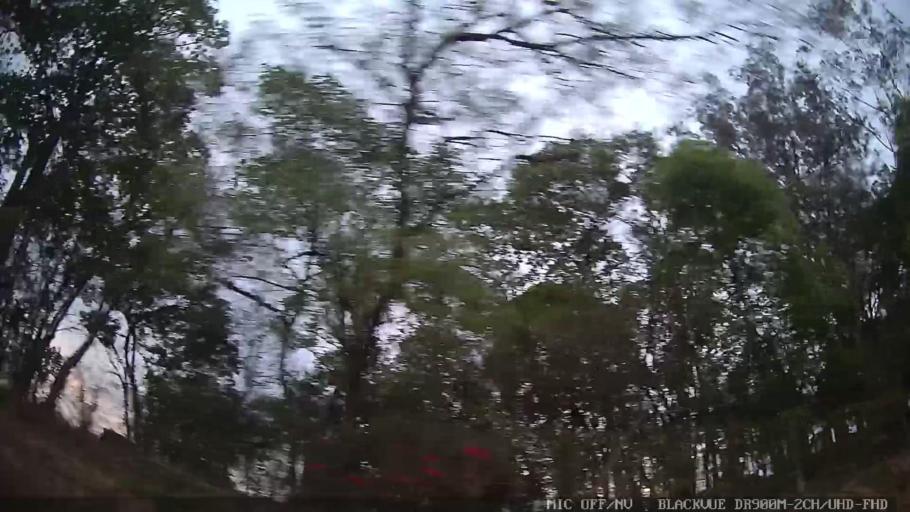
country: BR
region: Sao Paulo
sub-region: Louveira
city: Louveira
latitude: -23.1271
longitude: -46.9665
